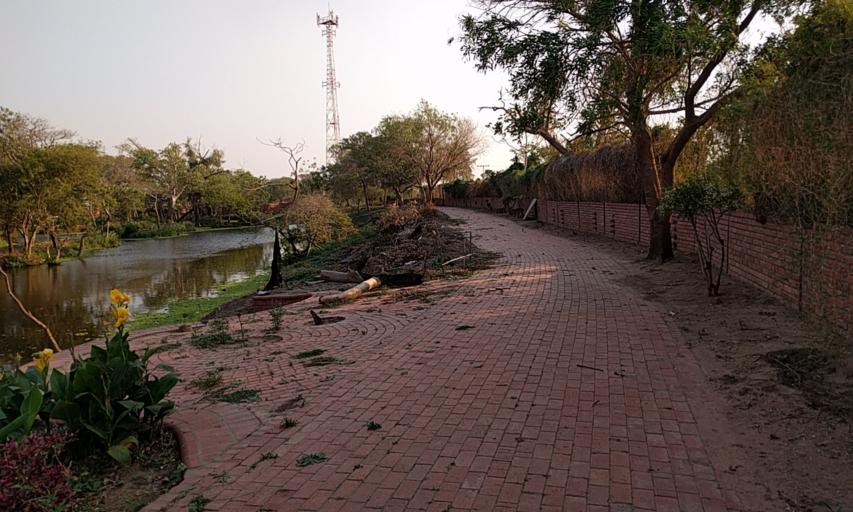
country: BO
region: Santa Cruz
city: Warnes
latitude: -17.4482
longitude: -63.1863
